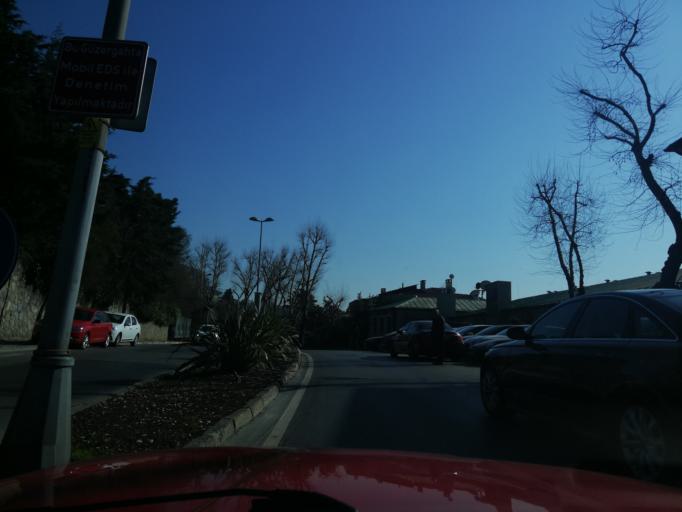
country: TR
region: Istanbul
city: UEskuedar
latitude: 41.0543
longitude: 29.0521
